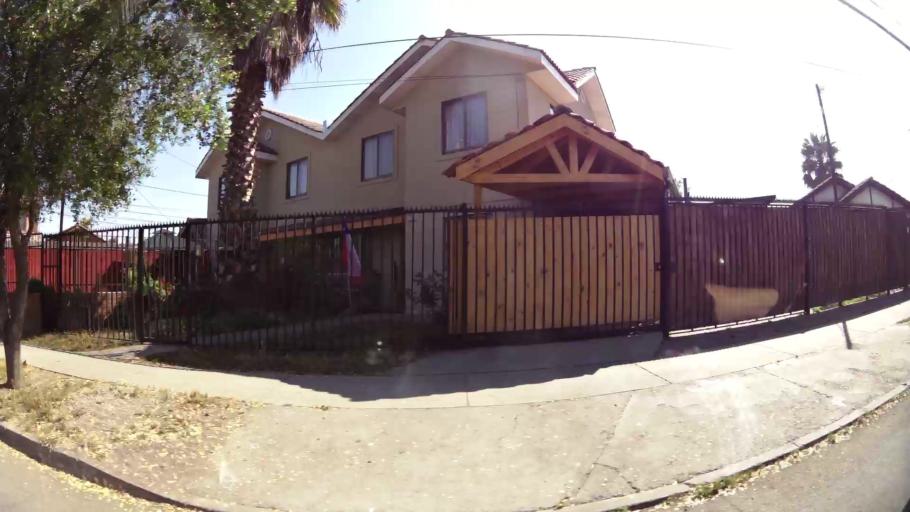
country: CL
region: Santiago Metropolitan
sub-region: Provincia de Santiago
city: Lo Prado
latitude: -33.3515
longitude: -70.7324
